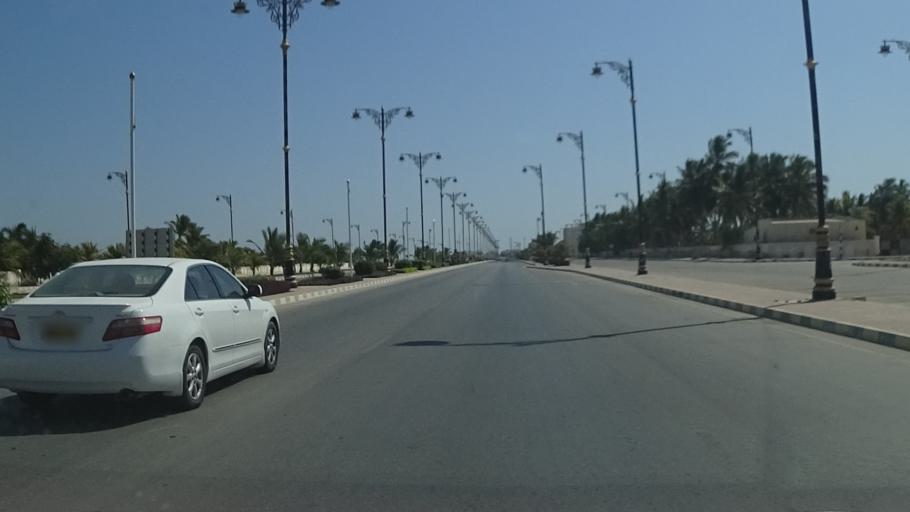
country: OM
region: Zufar
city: Salalah
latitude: 17.0347
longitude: 54.1719
